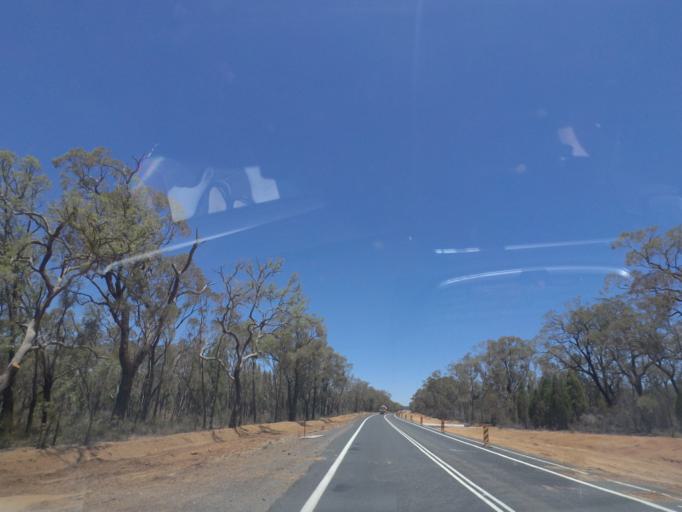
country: AU
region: New South Wales
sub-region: Warrumbungle Shire
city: Coonabarabran
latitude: -30.9248
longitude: 149.4314
